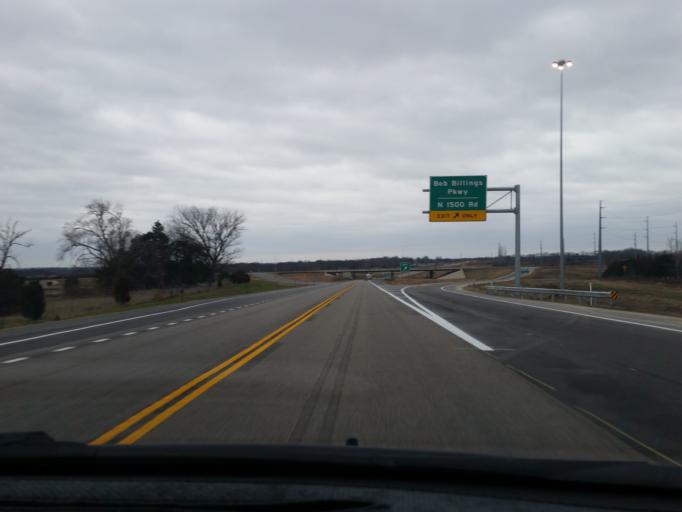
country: US
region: Kansas
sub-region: Douglas County
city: Lawrence
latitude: 38.9647
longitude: -95.3342
